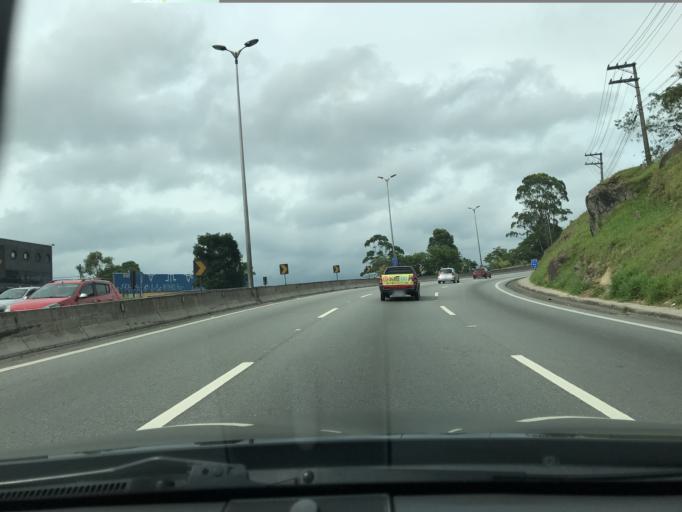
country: BR
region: Sao Paulo
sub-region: Cotia
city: Cotia
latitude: -23.5996
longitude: -46.8819
